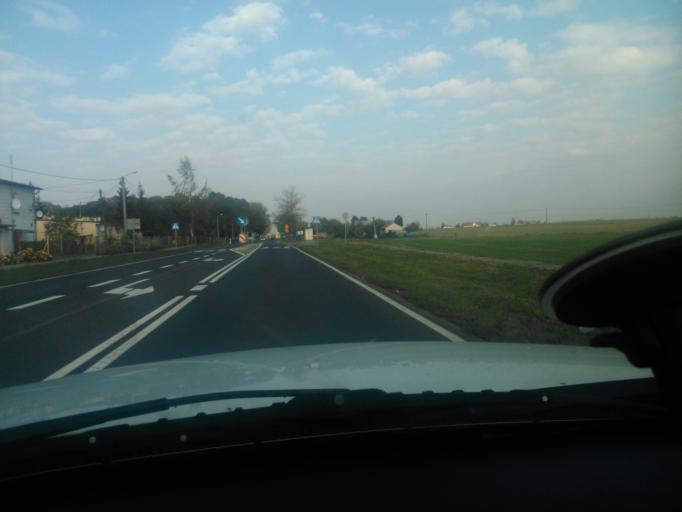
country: PL
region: Kujawsko-Pomorskie
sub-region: Powiat golubsko-dobrzynski
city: Kowalewo Pomorskie
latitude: 53.1619
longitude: 18.9187
